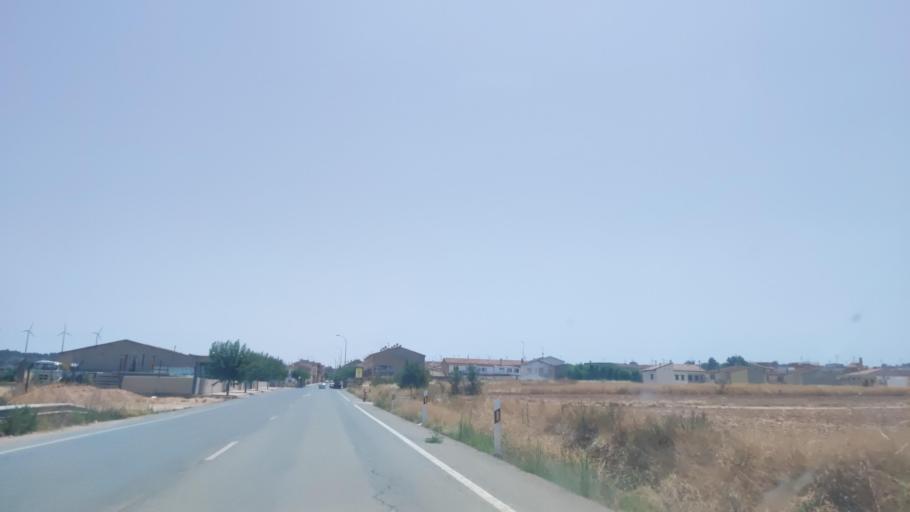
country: ES
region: Castille-La Mancha
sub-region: Provincia de Albacete
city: Pozo-Canada
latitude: 38.8079
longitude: -1.7360
